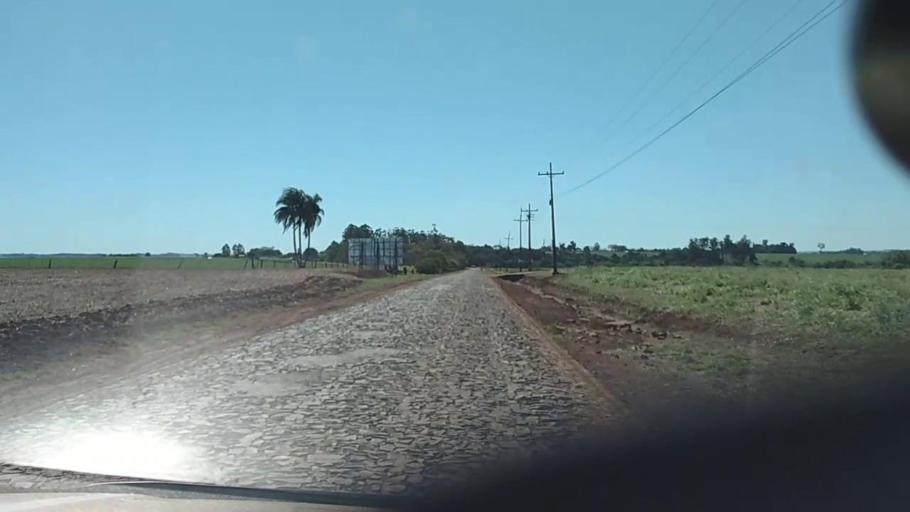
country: PY
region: Alto Parana
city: Naranjal
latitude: -25.9669
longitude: -55.1471
